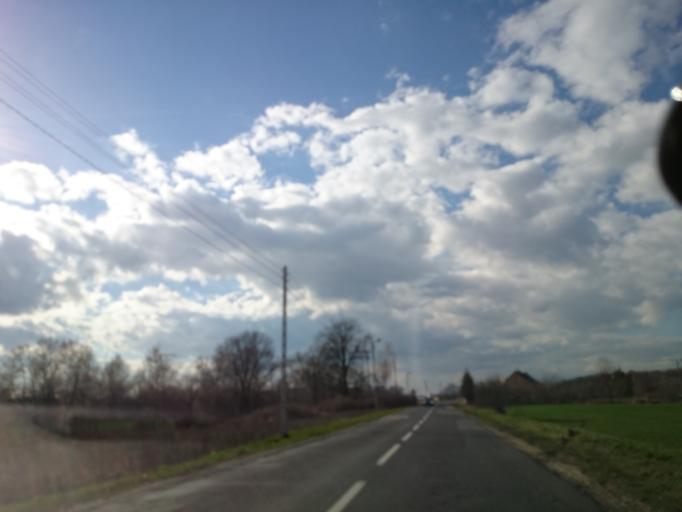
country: PL
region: Opole Voivodeship
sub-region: Powiat nyski
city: Sidzina
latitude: 50.6432
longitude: 17.4862
